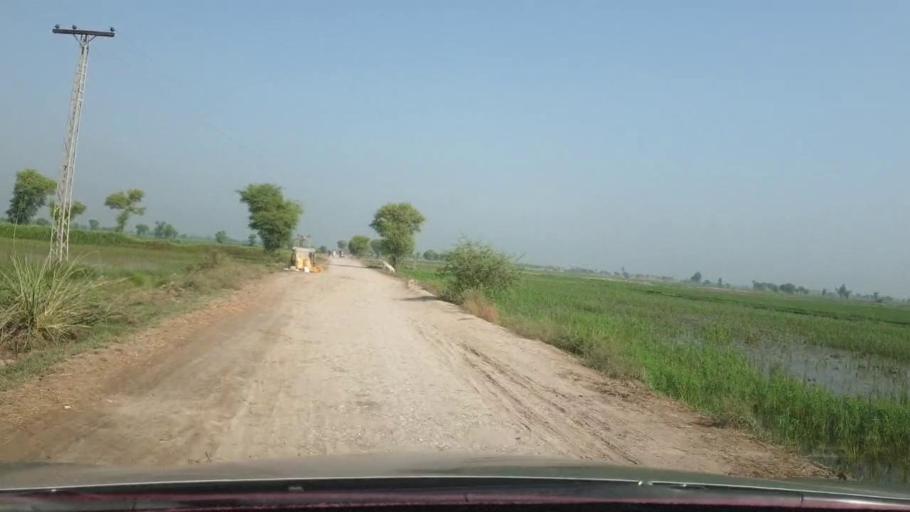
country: PK
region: Sindh
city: Kambar
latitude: 27.5913
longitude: 67.9386
